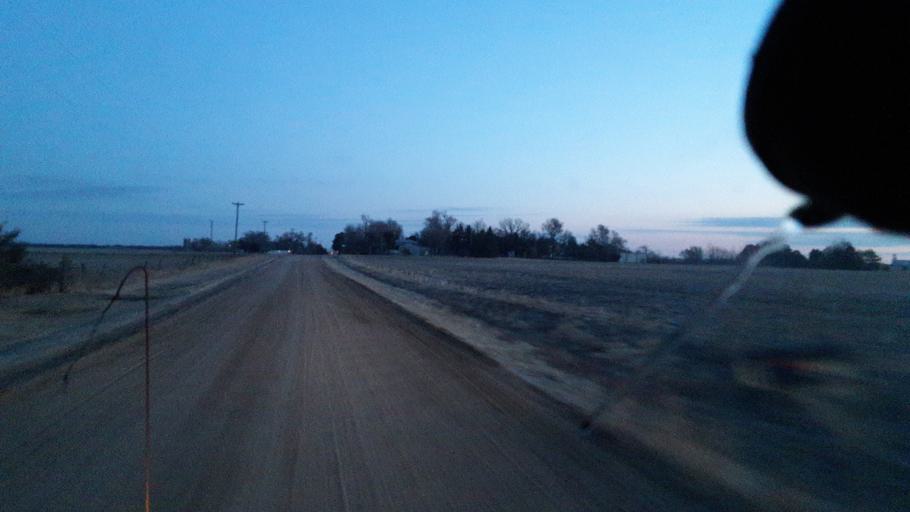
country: US
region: Kansas
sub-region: Reno County
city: South Hutchinson
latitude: 37.9975
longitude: -97.9770
